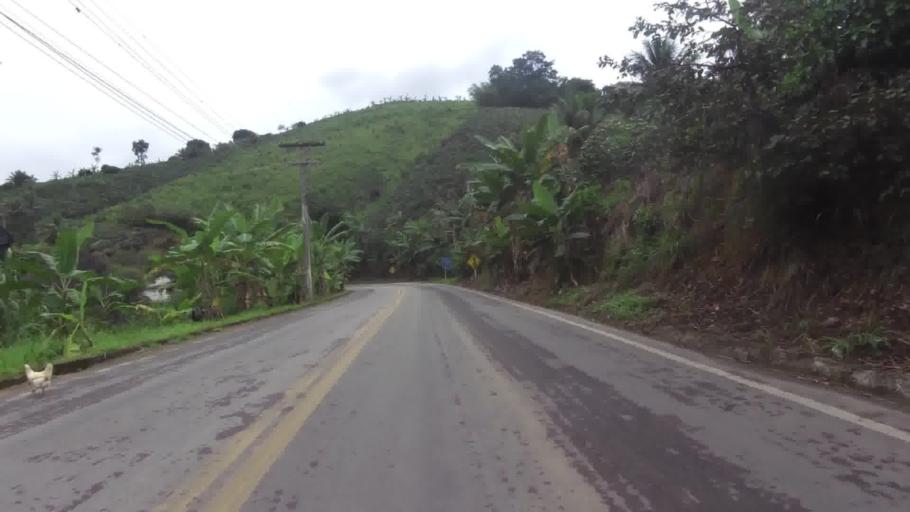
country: BR
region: Espirito Santo
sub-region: Iconha
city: Iconha
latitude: -20.7590
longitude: -40.8365
